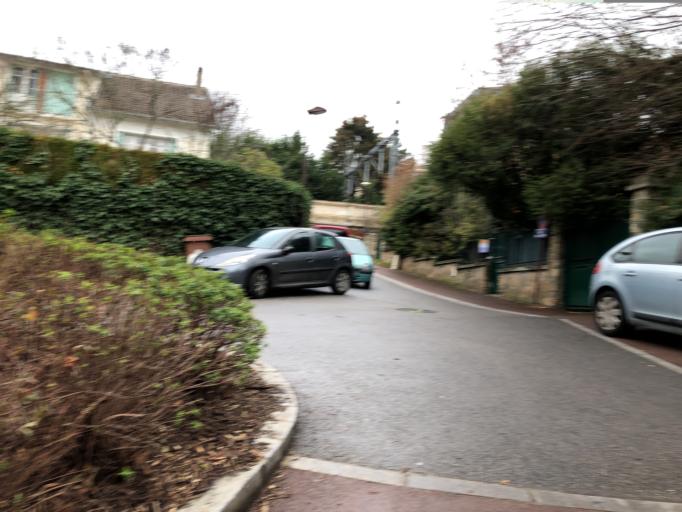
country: FR
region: Ile-de-France
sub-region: Departement des Hauts-de-Seine
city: Chaville
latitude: 48.8052
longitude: 2.1759
